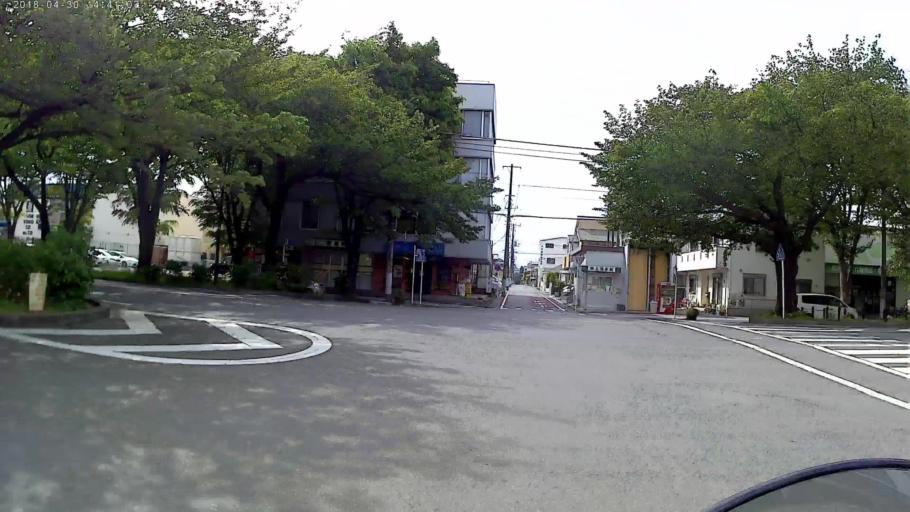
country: JP
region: Kanagawa
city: Zama
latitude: 35.5658
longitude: 139.3704
